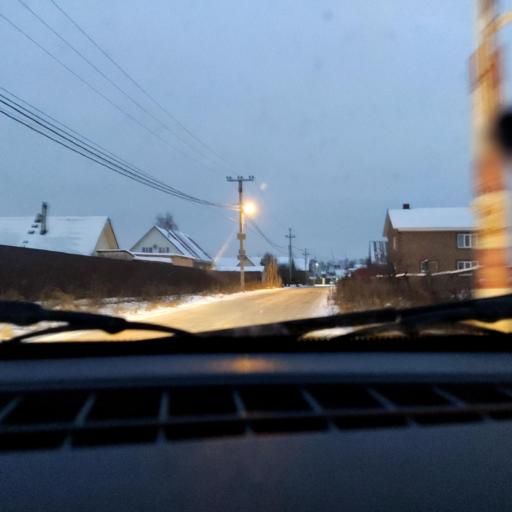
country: RU
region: Bashkortostan
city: Ufa
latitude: 54.6766
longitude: 56.0907
